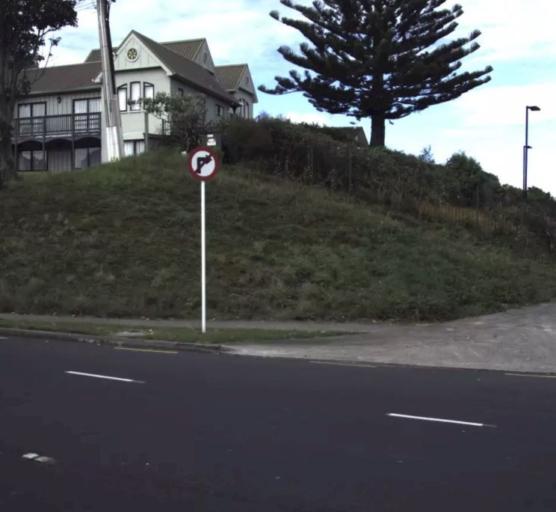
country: NZ
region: Auckland
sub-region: Auckland
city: Manukau City
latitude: -36.9915
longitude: 174.8901
